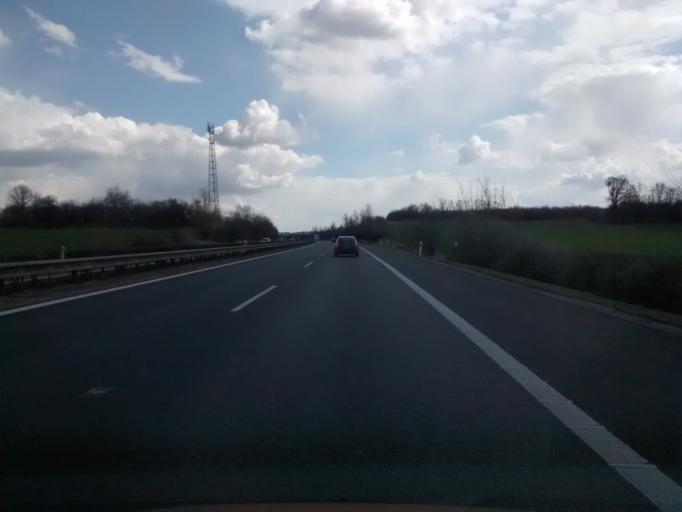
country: CZ
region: Central Bohemia
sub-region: Okres Melnik
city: Veltrusy
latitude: 50.2732
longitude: 14.3572
